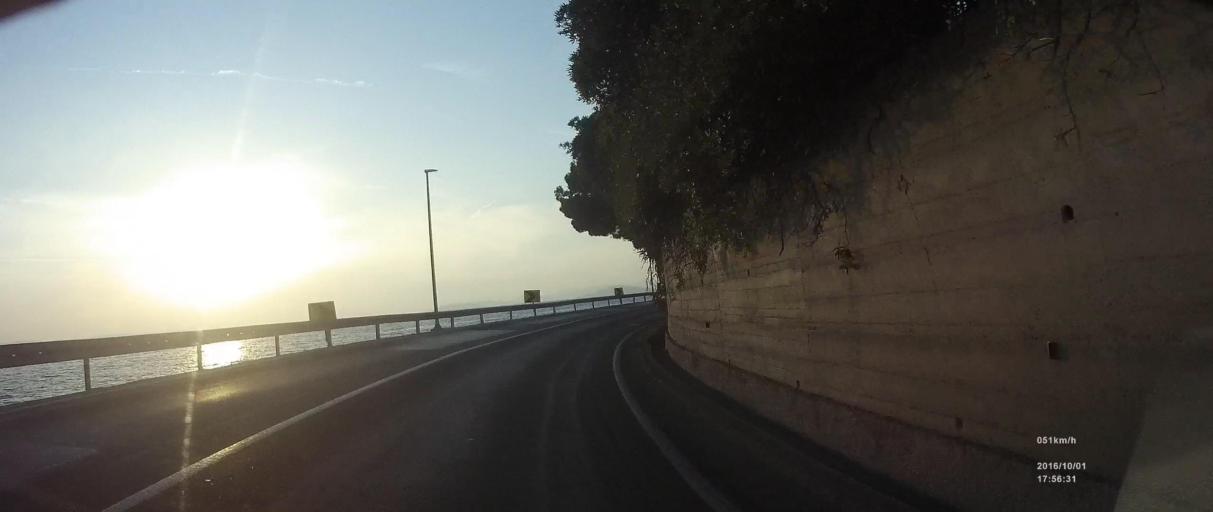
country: HR
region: Splitsko-Dalmatinska
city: Srinjine
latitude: 43.4645
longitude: 16.5819
